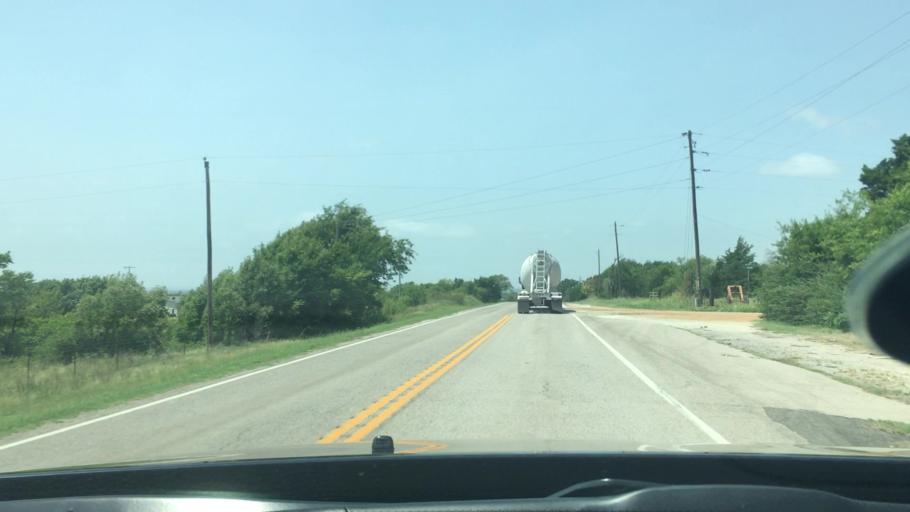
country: US
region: Oklahoma
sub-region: Murray County
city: Sulphur
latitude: 34.5109
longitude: -96.9319
